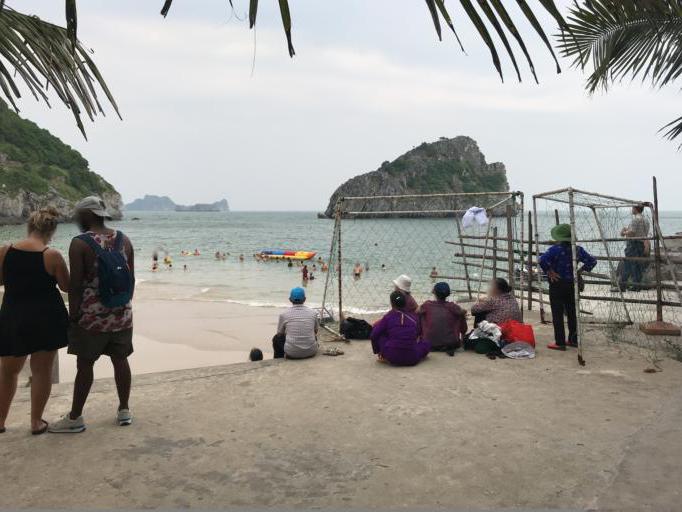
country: VN
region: Hai Phong
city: Cat Ba
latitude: 20.7154
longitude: 107.0492
